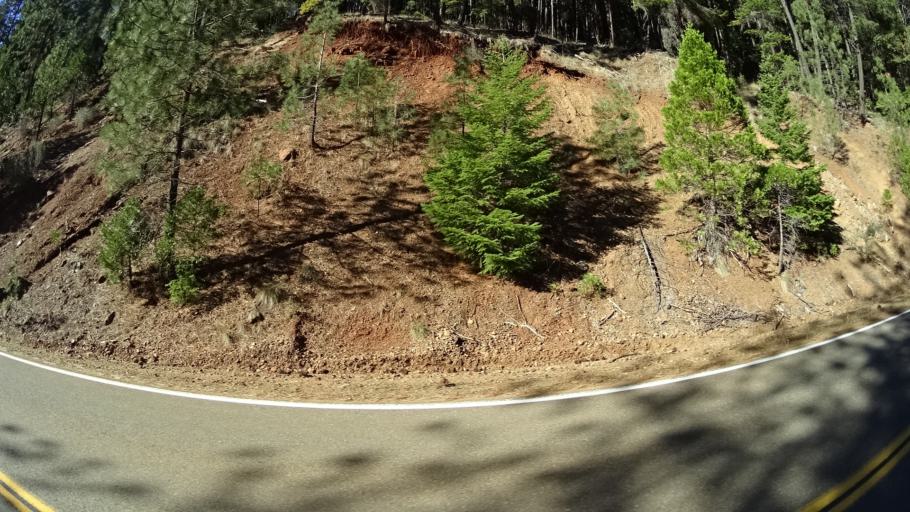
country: US
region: California
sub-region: Trinity County
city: Weaverville
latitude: 41.1504
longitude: -123.1204
